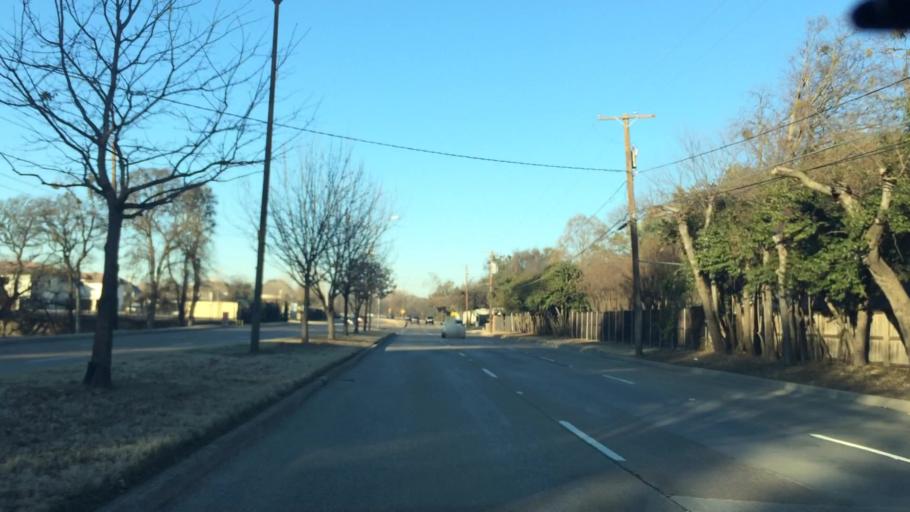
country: US
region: Texas
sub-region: Dallas County
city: Addison
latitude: 32.9400
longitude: -96.7915
